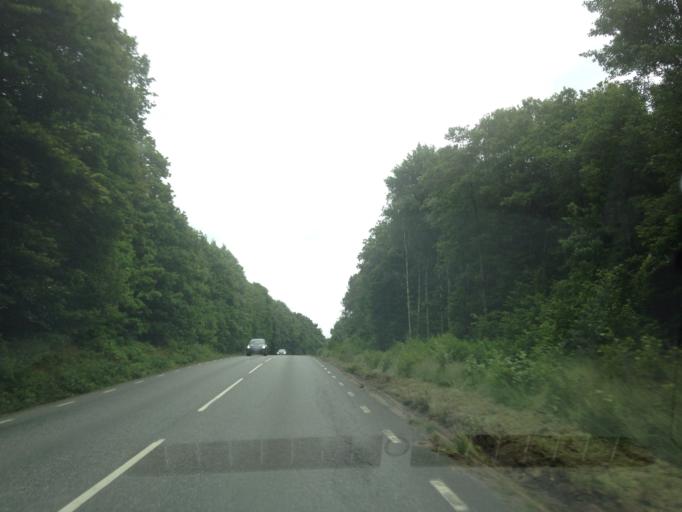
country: SE
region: Vaestra Goetaland
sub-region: Kungalvs Kommun
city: Kode
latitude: 57.8574
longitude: 11.8526
